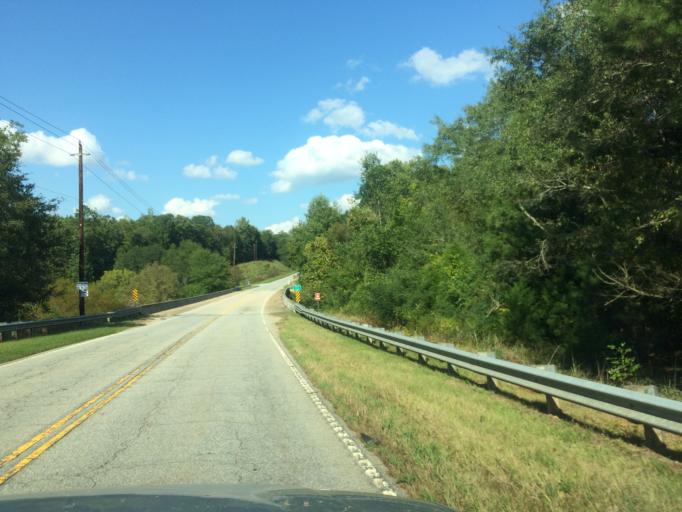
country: US
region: South Carolina
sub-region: Greenwood County
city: Ware Shoals
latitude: 34.4546
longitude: -82.1982
